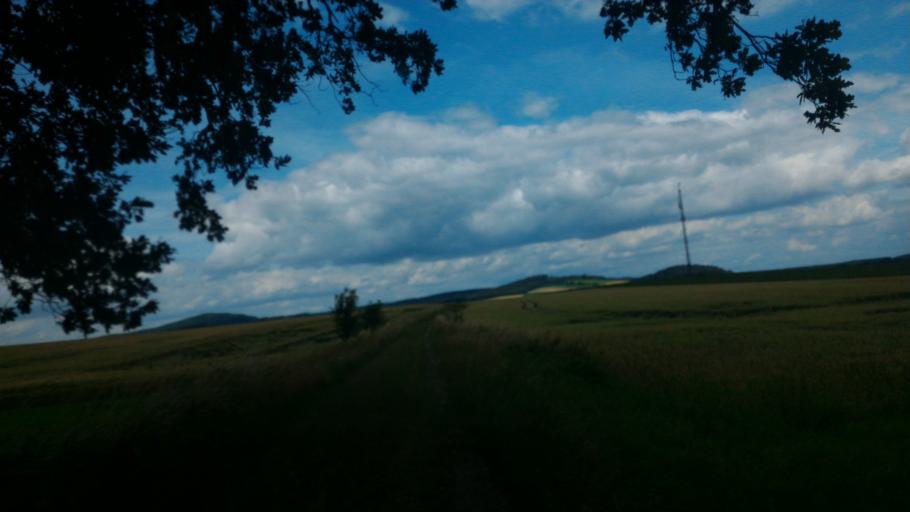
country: DE
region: Saxony
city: Grossschonau
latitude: 50.8849
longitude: 14.6793
